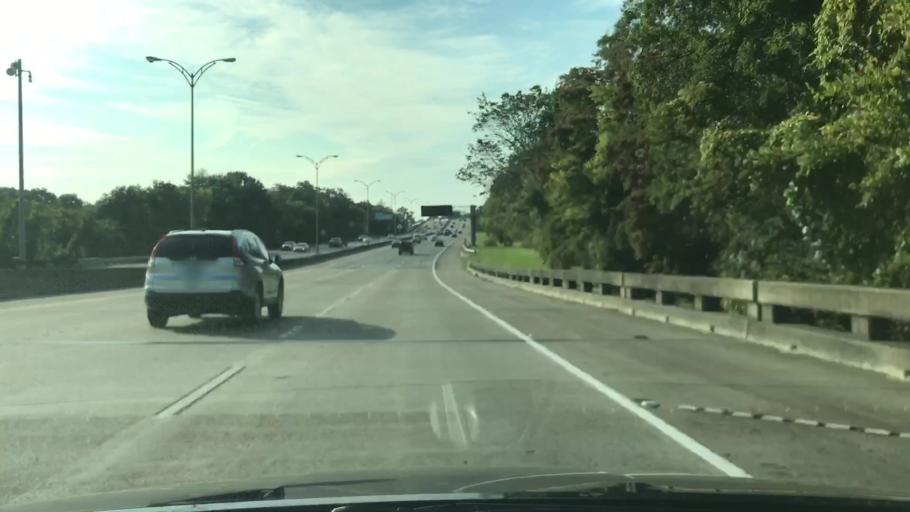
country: US
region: Louisiana
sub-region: Orleans Parish
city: New Orleans
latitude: 29.9938
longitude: -90.0939
